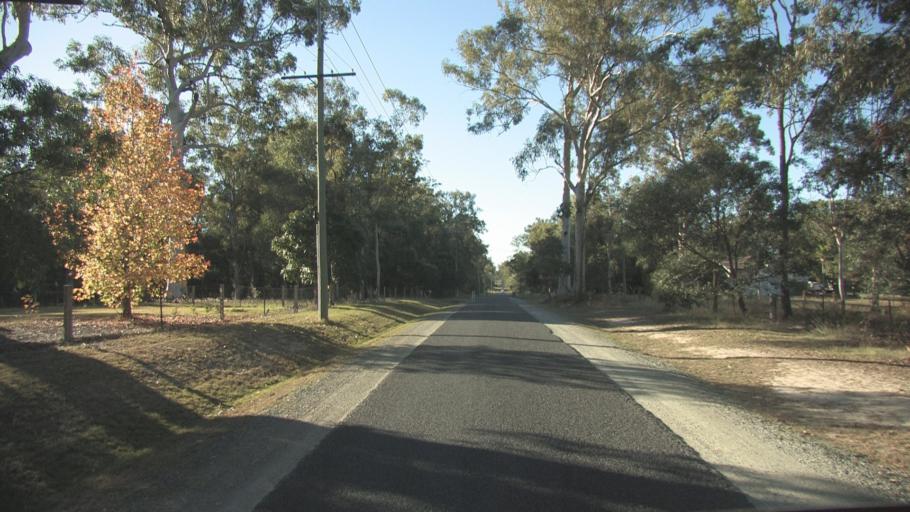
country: AU
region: Queensland
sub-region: Logan
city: Chambers Flat
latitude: -27.7871
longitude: 153.0861
